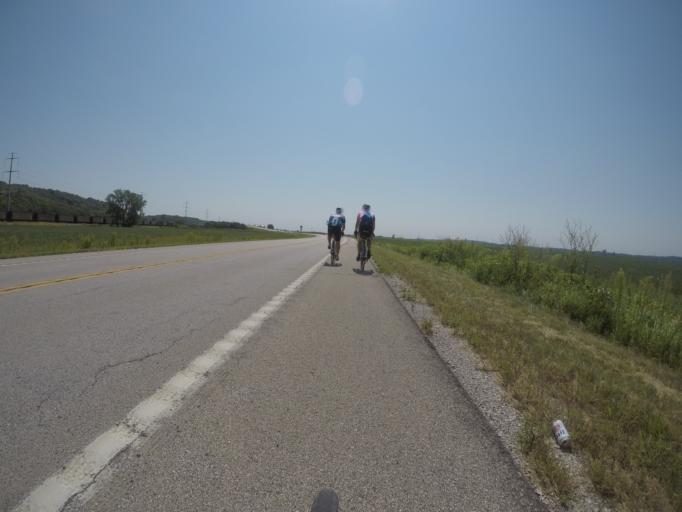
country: US
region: Missouri
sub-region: Platte County
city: Weston
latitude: 39.4419
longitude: -94.9473
